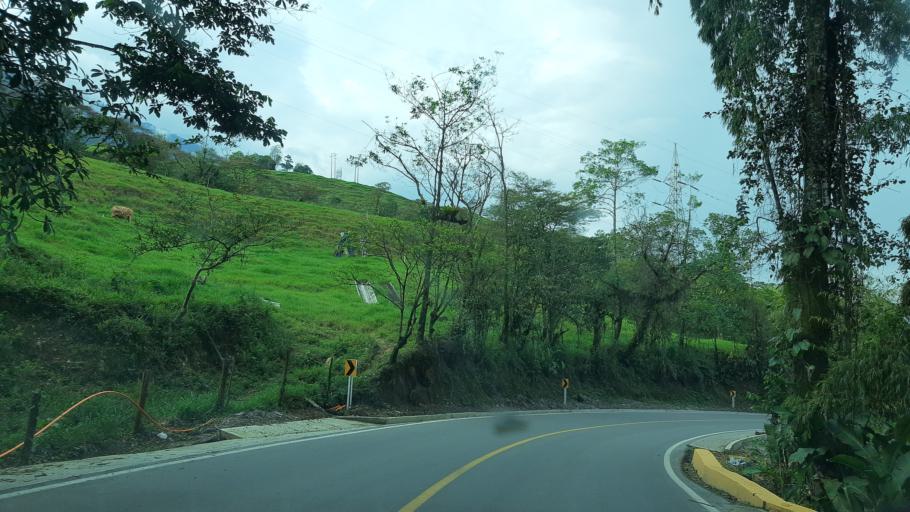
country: CO
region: Boyaca
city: Santa Maria
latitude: 4.8639
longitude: -73.2526
